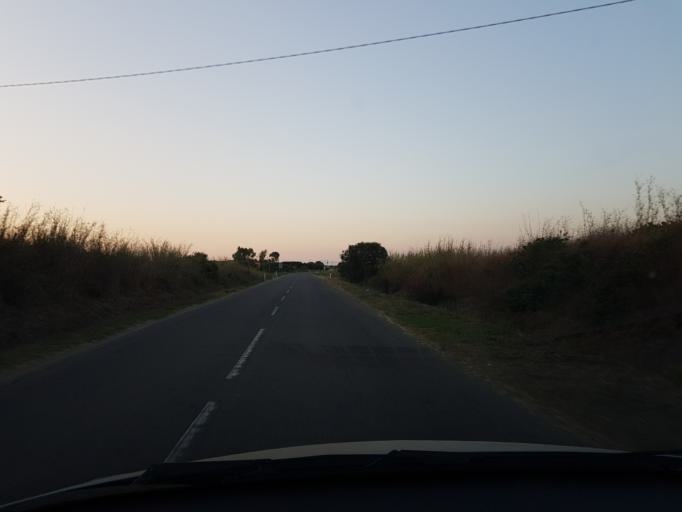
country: IT
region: Sardinia
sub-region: Provincia di Oristano
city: Nurachi
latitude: 39.9792
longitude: 8.4543
